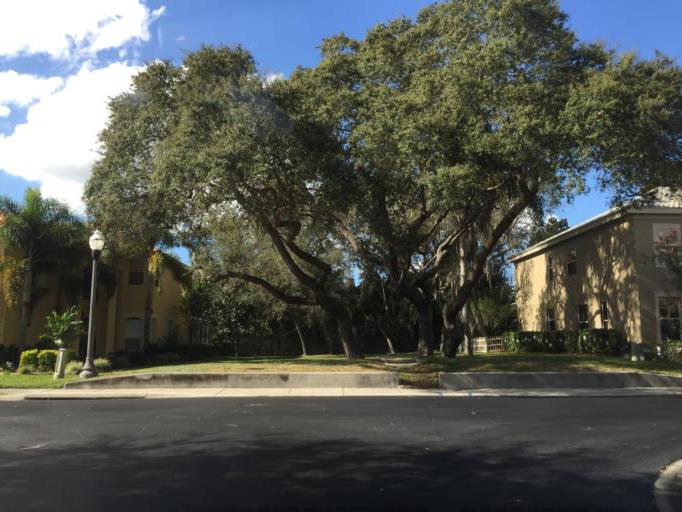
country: US
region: Florida
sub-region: Pinellas County
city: Saint George
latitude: 28.0453
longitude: -82.7464
